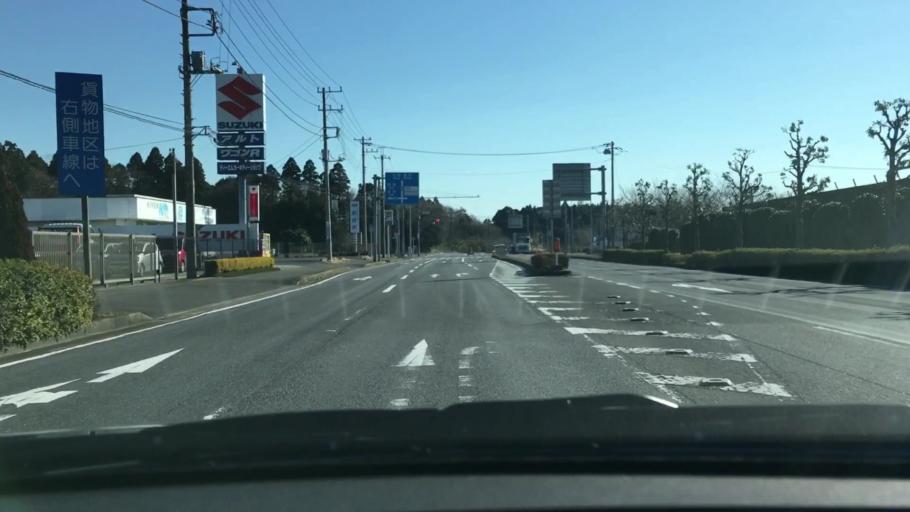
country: JP
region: Chiba
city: Narita
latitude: 35.7471
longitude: 140.4024
